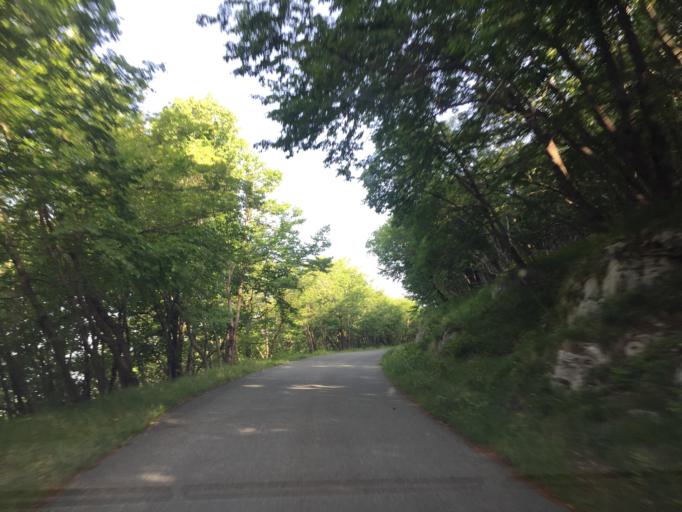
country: HR
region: Primorsko-Goranska
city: Klana
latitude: 45.4888
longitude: 14.4146
